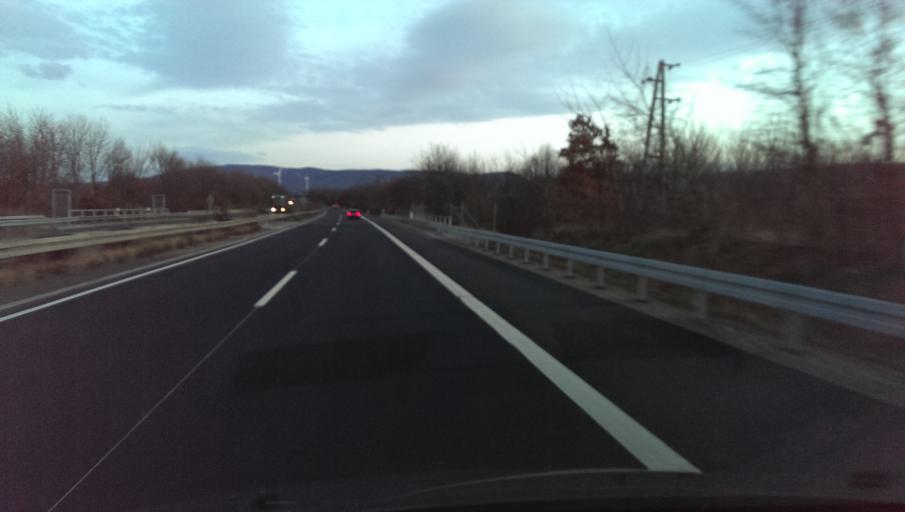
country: DE
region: Lower Saxony
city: Bad Harzburg
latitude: 51.9168
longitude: 10.5228
